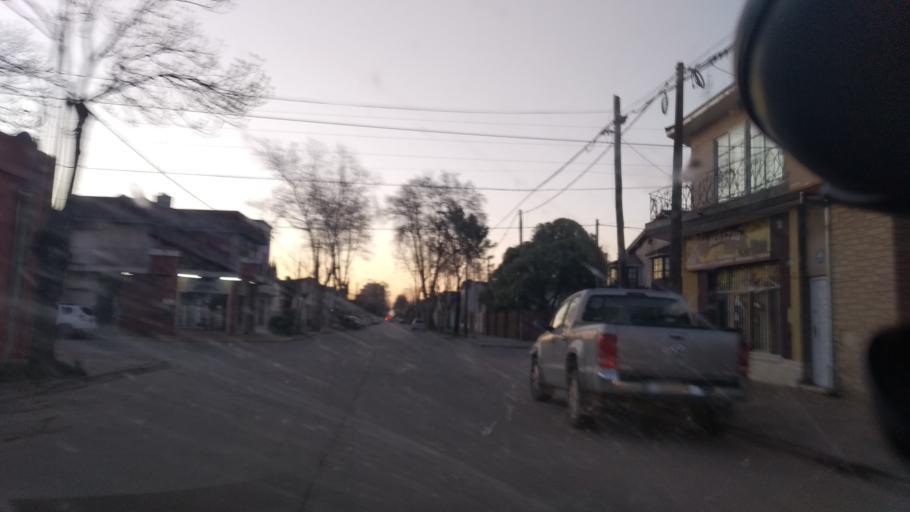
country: AR
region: Buenos Aires
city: Necochea
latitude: -38.5594
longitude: -58.7371
